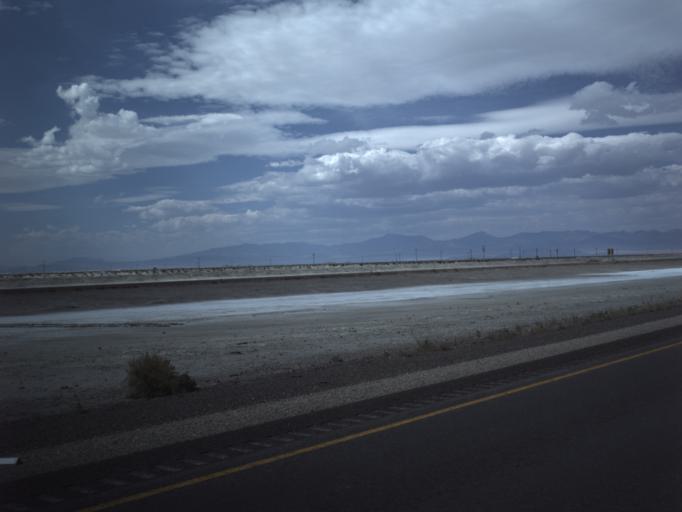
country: US
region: Utah
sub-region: Tooele County
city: Wendover
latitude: 40.7386
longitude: -113.8101
